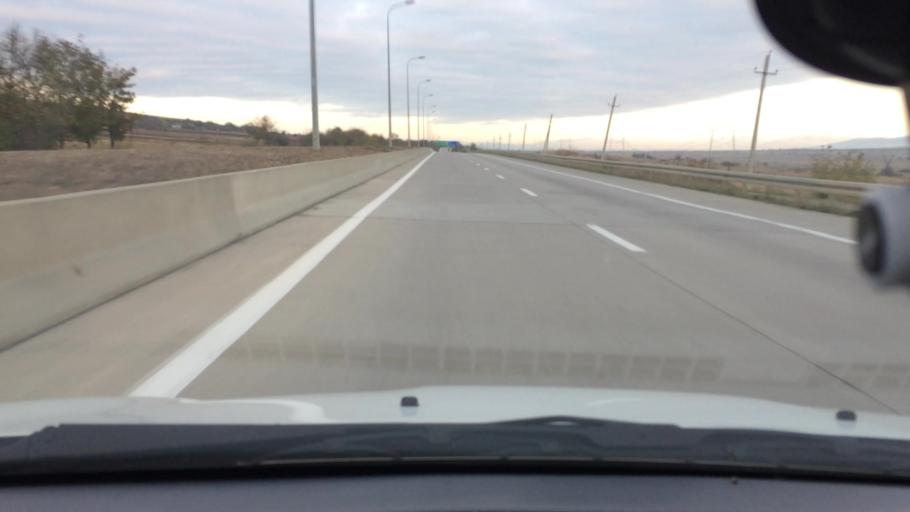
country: GE
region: Shida Kartli
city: Kaspi
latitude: 42.0093
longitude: 44.3412
